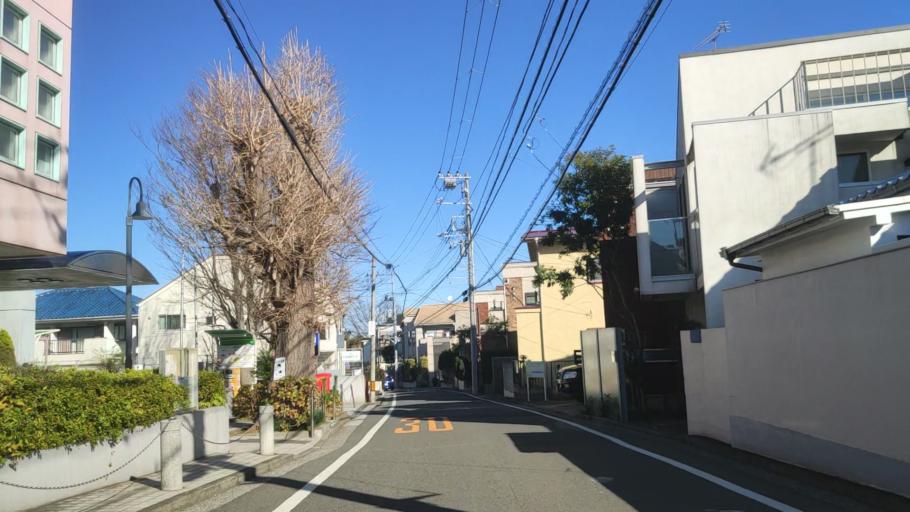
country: JP
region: Kanagawa
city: Yokohama
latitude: 35.4302
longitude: 139.6447
